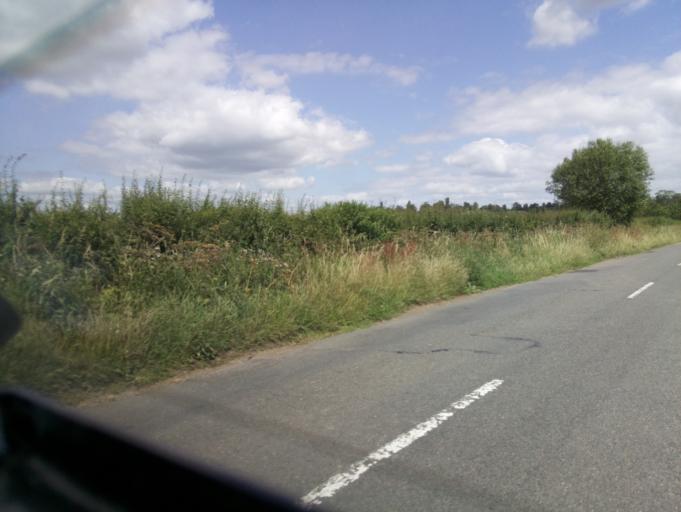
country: GB
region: England
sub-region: Buckinghamshire
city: Winslow
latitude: 51.9280
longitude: -0.8358
